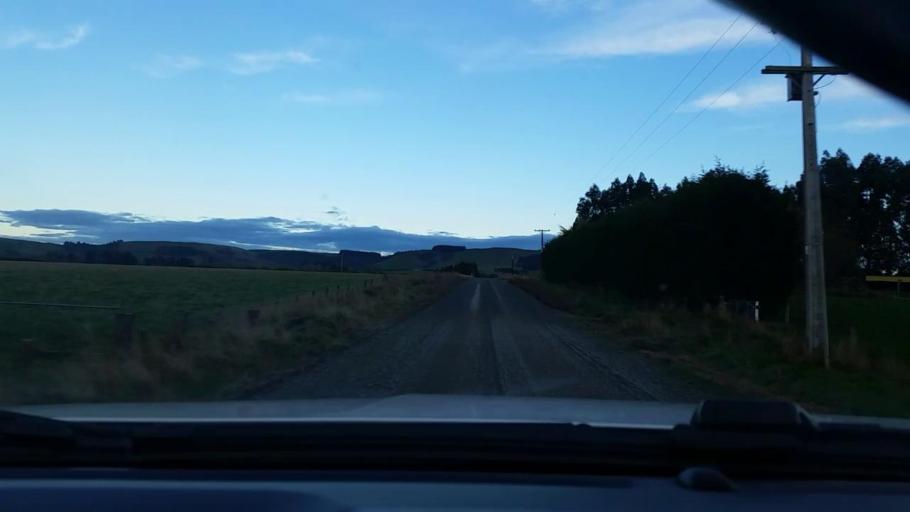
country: NZ
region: Southland
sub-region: Southland District
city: Winton
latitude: -46.1089
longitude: 168.4404
